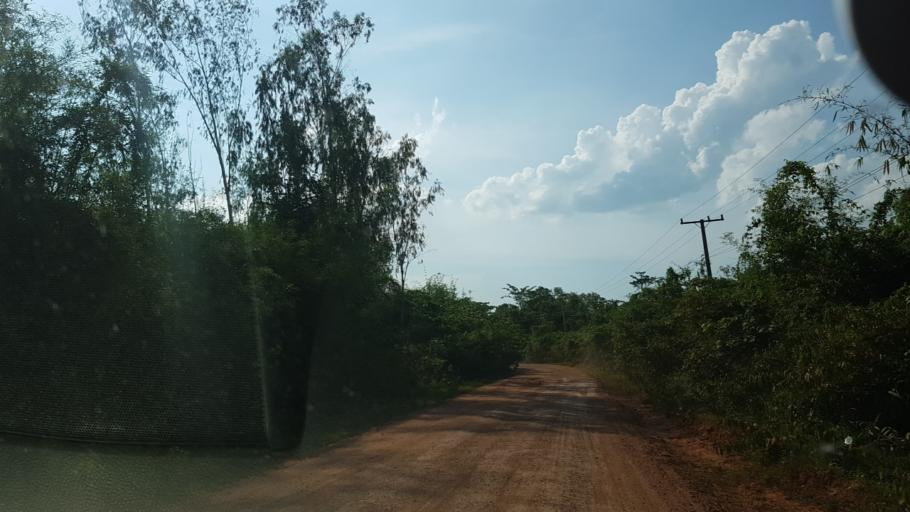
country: LA
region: Vientiane
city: Muang Phon-Hong
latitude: 18.3461
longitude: 102.2887
